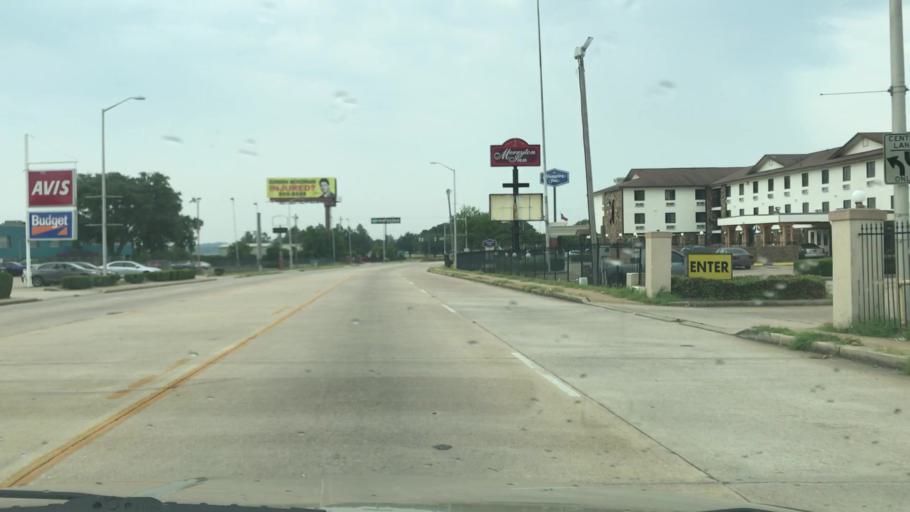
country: US
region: Louisiana
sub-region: Caddo Parish
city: Shreveport
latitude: 32.4589
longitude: -93.8274
